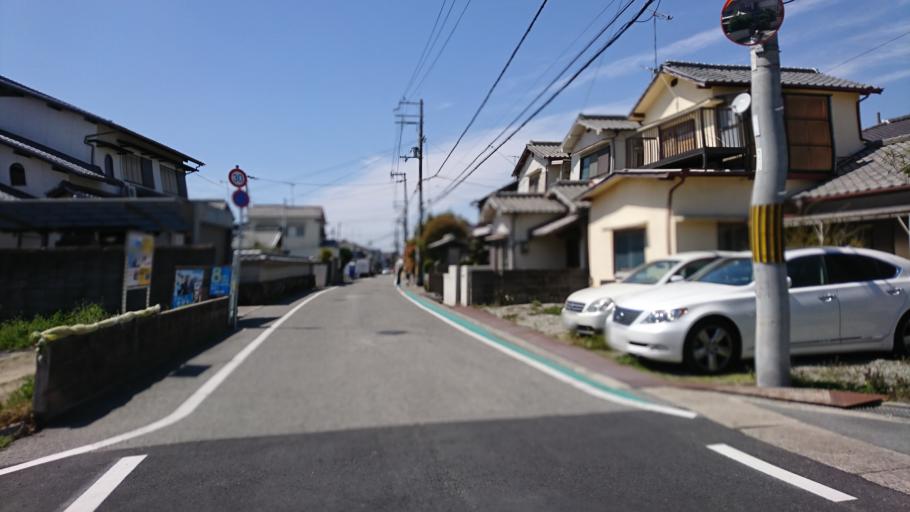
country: JP
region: Hyogo
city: Kakogawacho-honmachi
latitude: 34.7474
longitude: 134.8775
